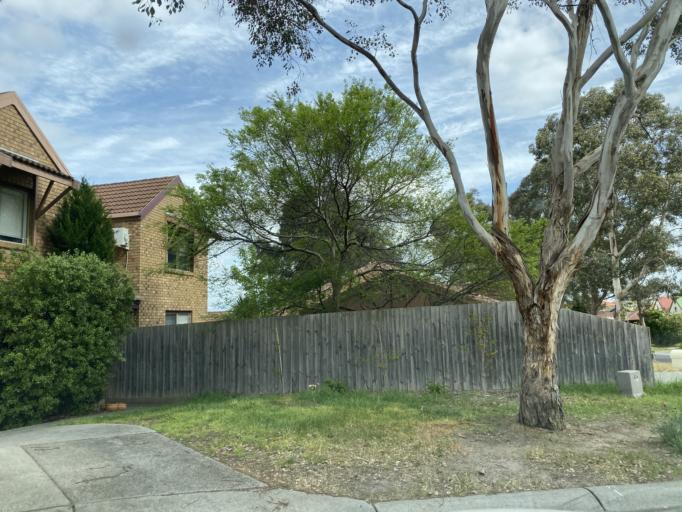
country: AU
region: Victoria
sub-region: Whitehorse
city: Burwood
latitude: -37.8426
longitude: 145.1061
